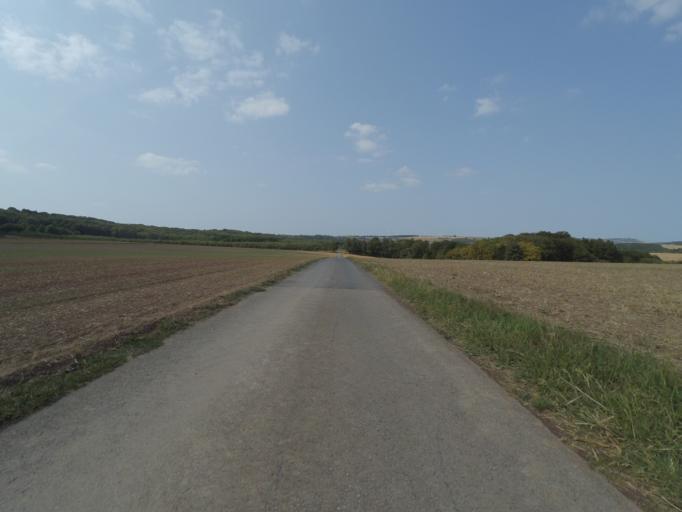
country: DE
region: Rheinland-Pfalz
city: Kirf
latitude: 49.5339
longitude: 6.4995
